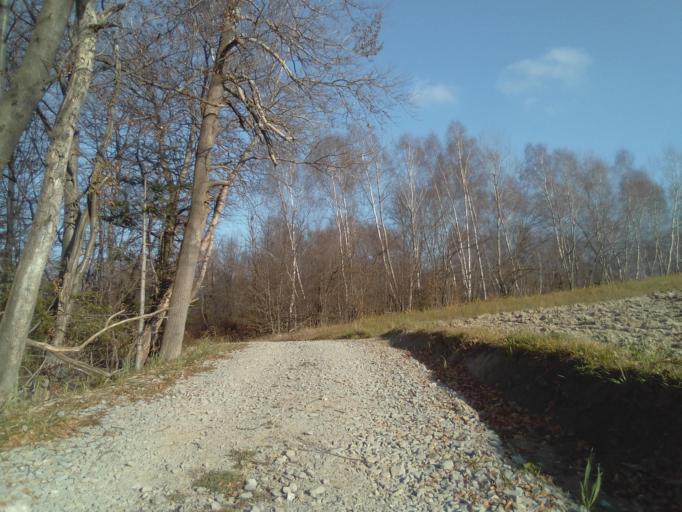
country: PL
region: Subcarpathian Voivodeship
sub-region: Powiat strzyzowski
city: Gwoznica Gorna
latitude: 49.8260
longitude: 21.9815
